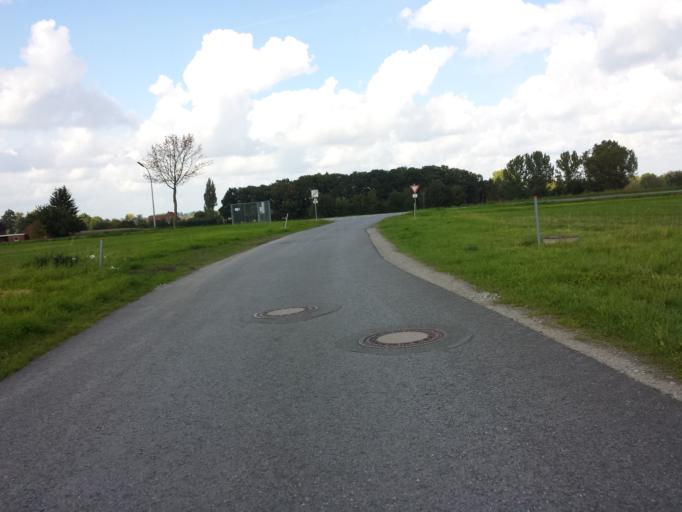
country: DE
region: North Rhine-Westphalia
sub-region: Regierungsbezirk Detmold
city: Langenberg
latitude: 51.7853
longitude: 8.3156
